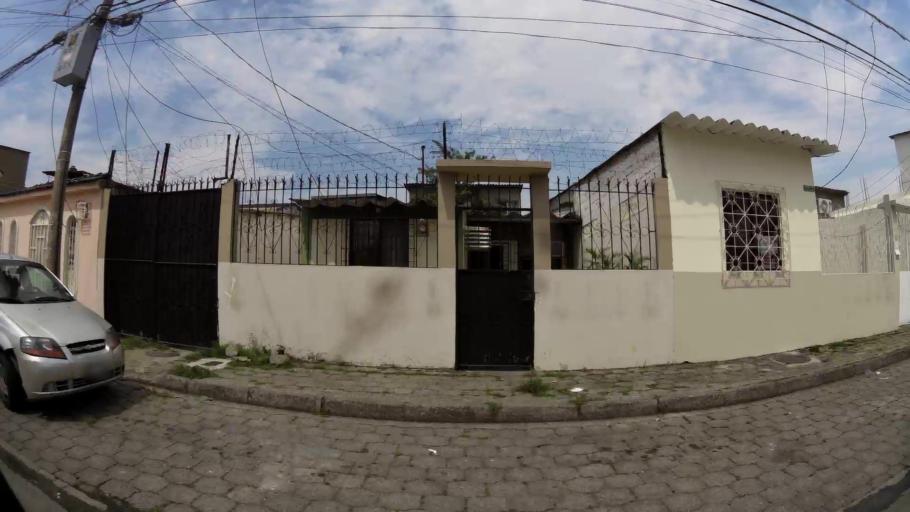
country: EC
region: Guayas
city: Eloy Alfaro
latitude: -2.1277
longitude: -79.9049
